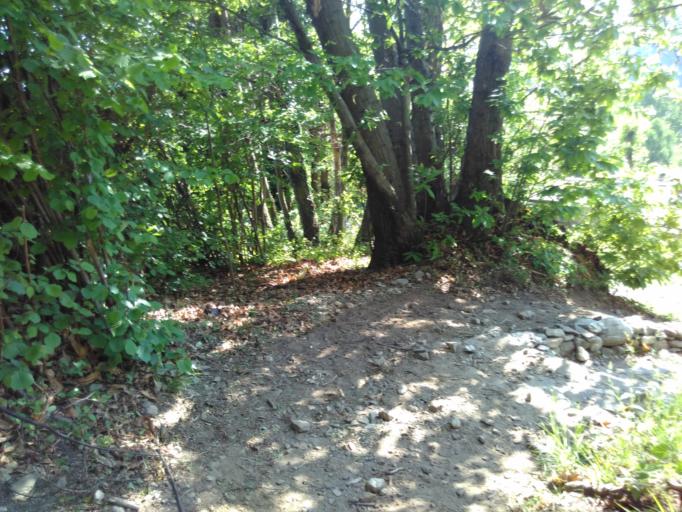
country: CH
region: Ticino
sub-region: Bellinzona District
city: Sementina
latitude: 46.1916
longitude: 8.9900
